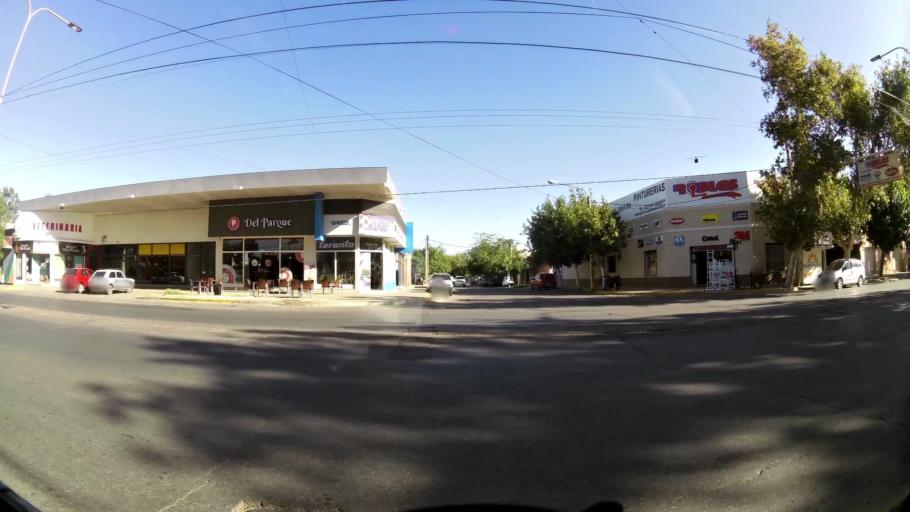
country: AR
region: San Juan
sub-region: Departamento de Santa Lucia
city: Santa Lucia
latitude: -31.5417
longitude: -68.5105
